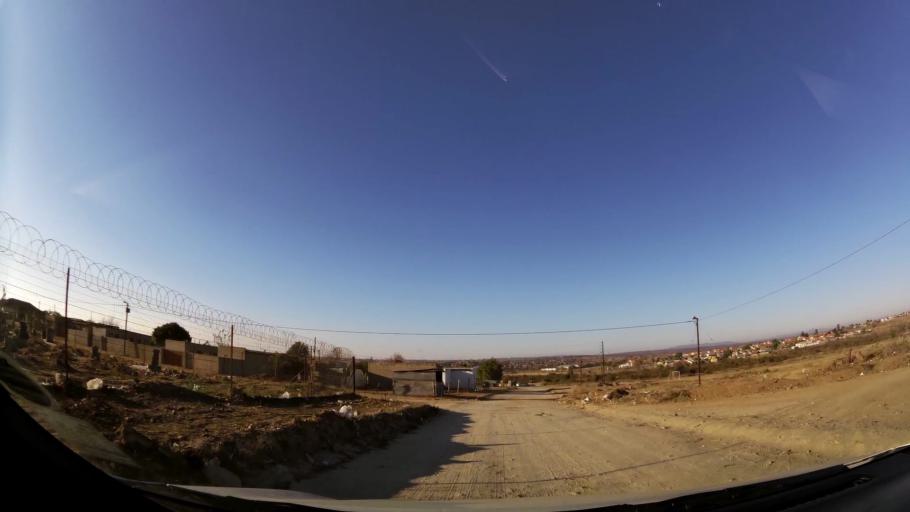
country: ZA
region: Limpopo
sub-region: Capricorn District Municipality
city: Polokwane
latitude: -23.8386
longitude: 29.3591
